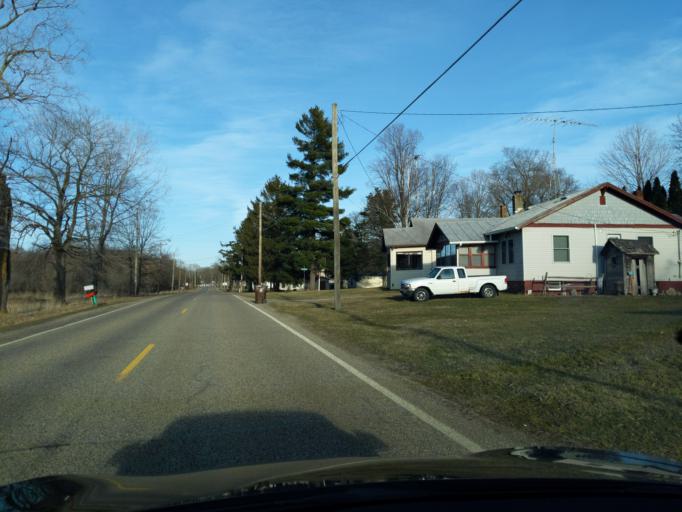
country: US
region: Michigan
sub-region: Ionia County
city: Ionia
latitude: 42.9659
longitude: -85.0799
